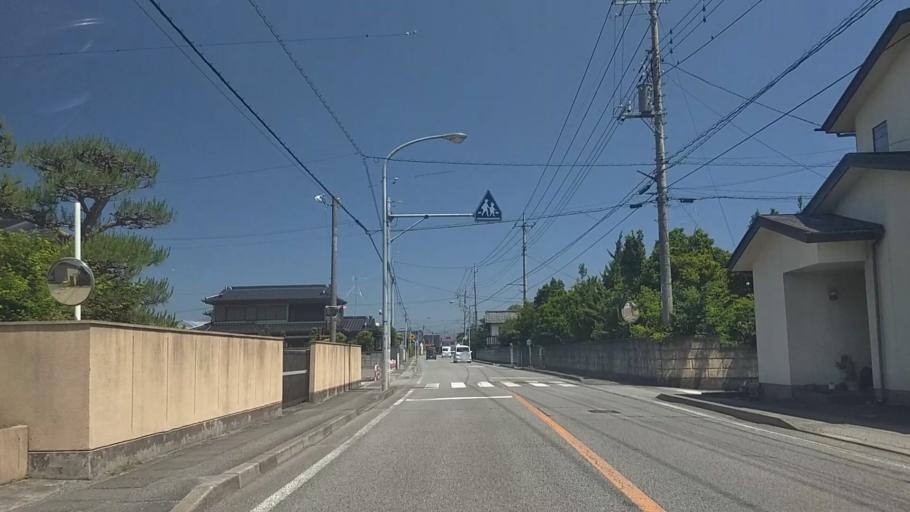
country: JP
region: Yamanashi
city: Ryuo
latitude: 35.6492
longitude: 138.4634
